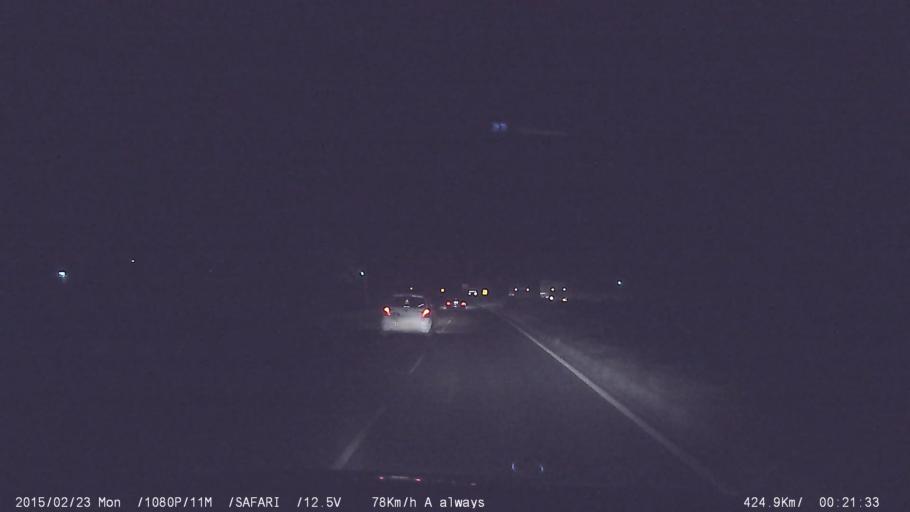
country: IN
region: Tamil Nadu
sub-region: Salem
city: Omalur
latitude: 11.9023
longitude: 78.0618
